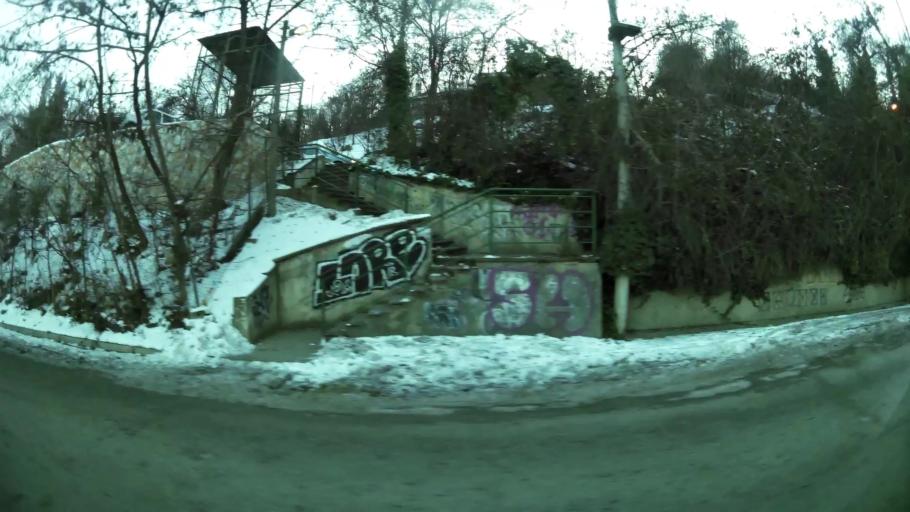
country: MK
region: Karpos
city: Skopje
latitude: 41.9917
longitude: 21.4121
